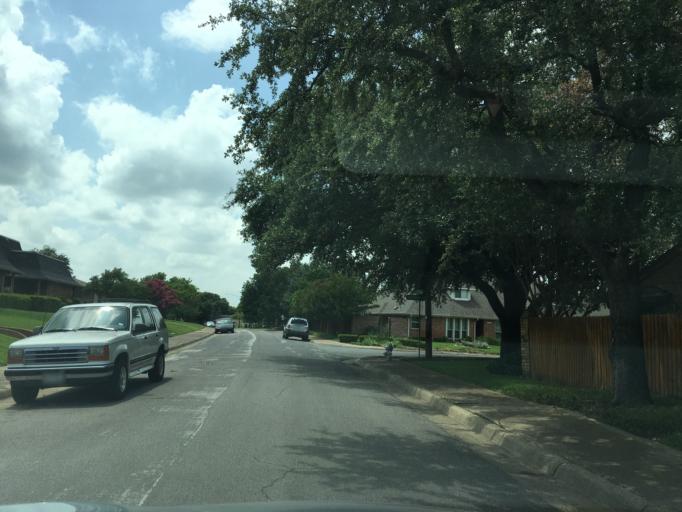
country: US
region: Texas
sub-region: Dallas County
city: University Park
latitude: 32.8890
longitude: -96.7763
